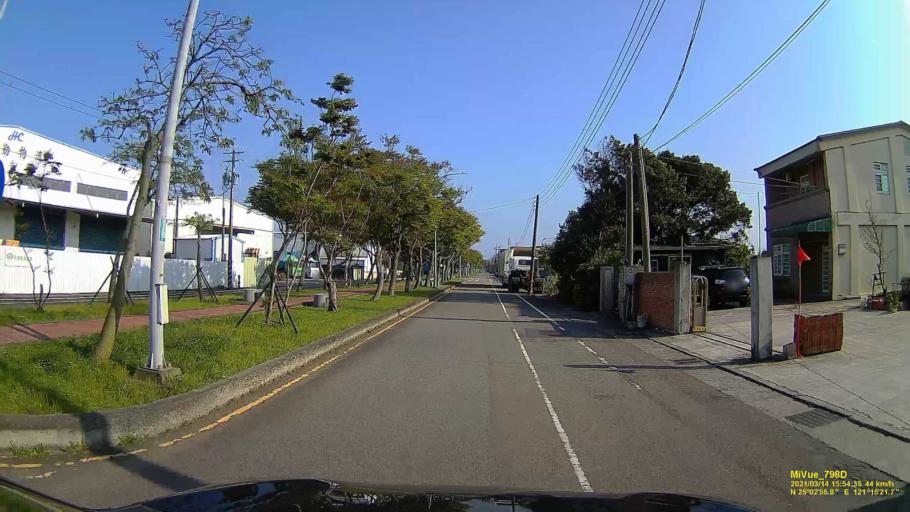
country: TW
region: Taiwan
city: Taoyuan City
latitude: 25.0487
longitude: 121.2561
